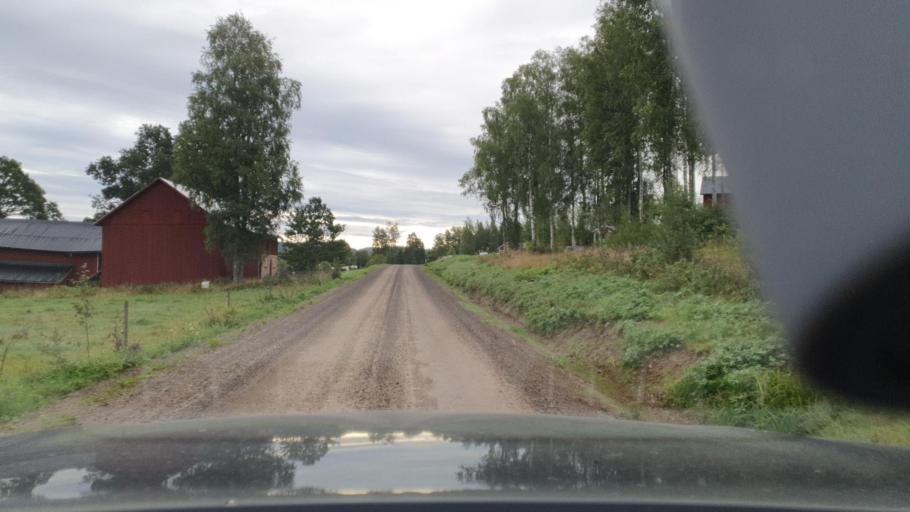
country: SE
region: Vaermland
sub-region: Torsby Kommun
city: Torsby
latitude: 59.9699
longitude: 12.8682
